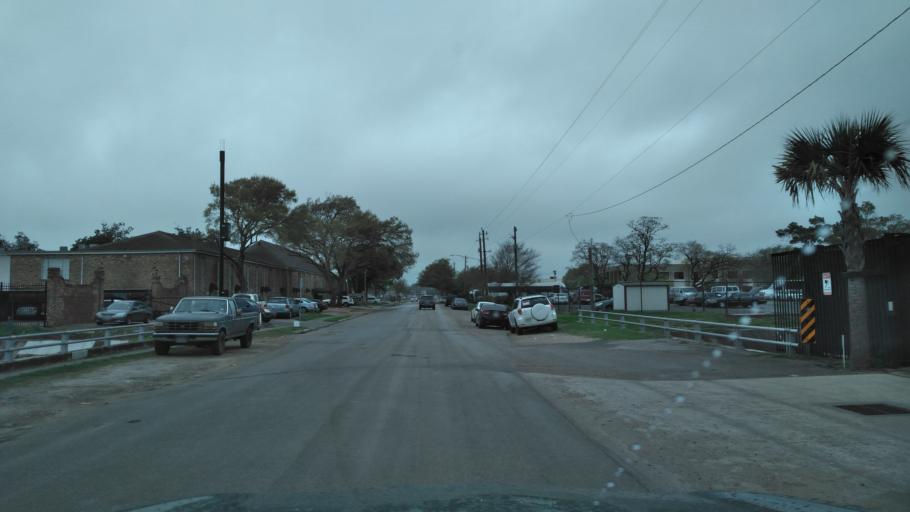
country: US
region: Texas
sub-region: Harris County
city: Piney Point Village
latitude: 29.7306
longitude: -95.4952
